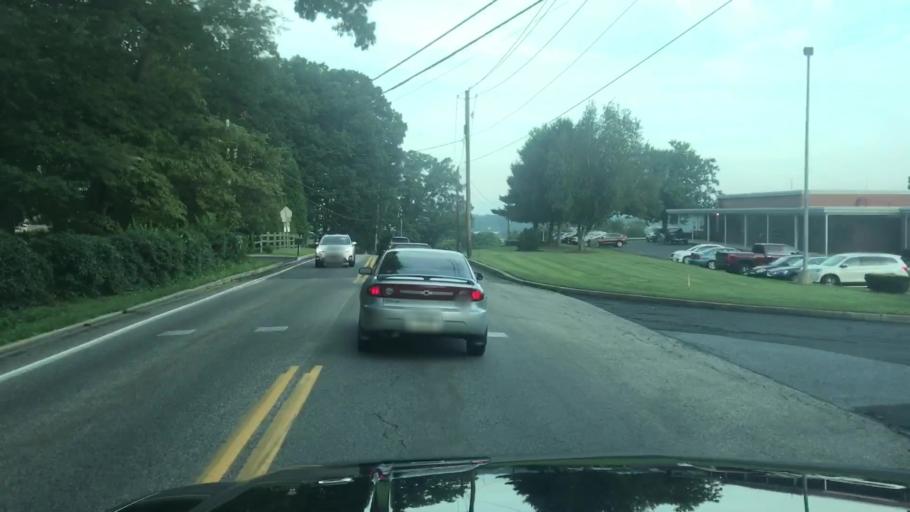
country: US
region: Pennsylvania
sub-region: Cumberland County
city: Shiremanstown
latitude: 40.2016
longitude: -76.9520
